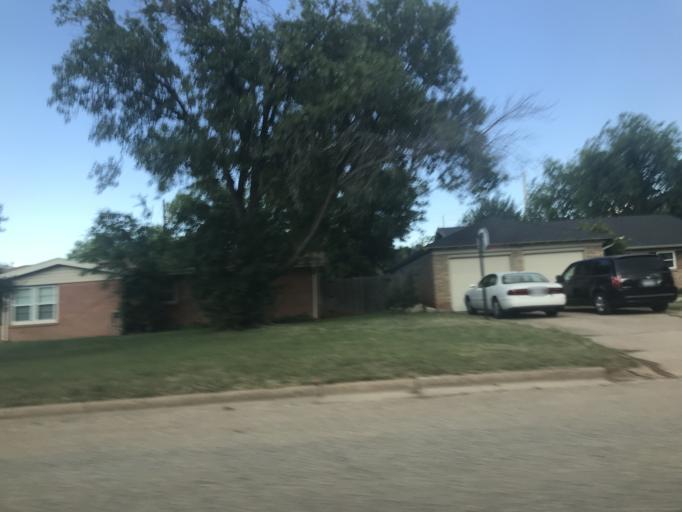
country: US
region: Texas
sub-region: Taylor County
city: Abilene
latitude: 32.4276
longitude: -99.7670
